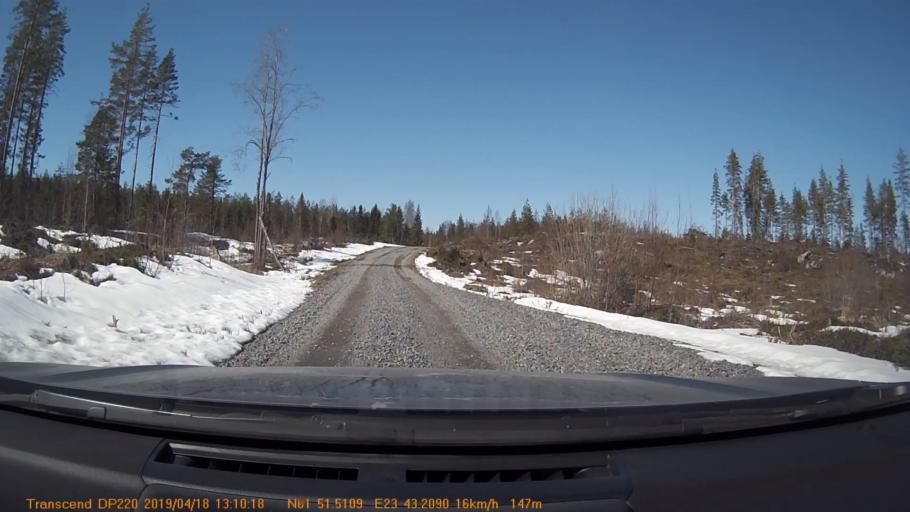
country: FI
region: Pirkanmaa
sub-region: Tampere
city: Kuru
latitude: 61.8585
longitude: 23.7202
